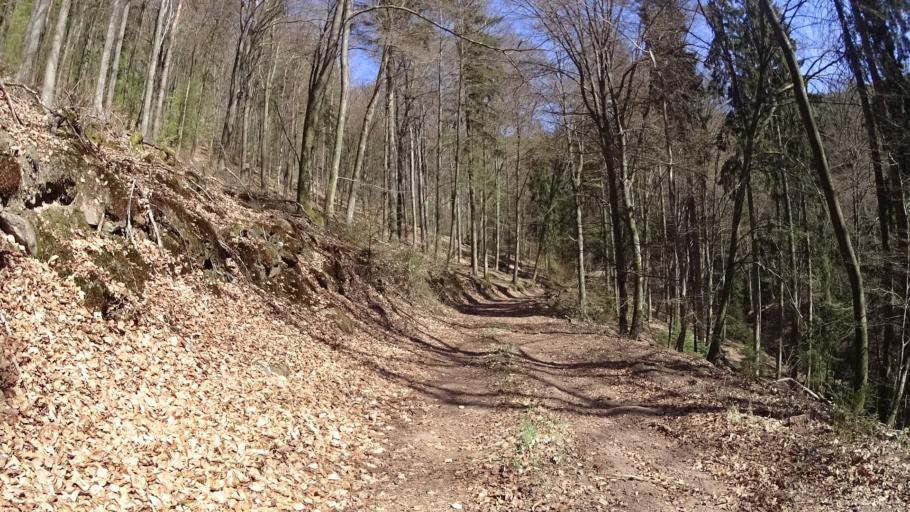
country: DE
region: Rheinland-Pfalz
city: Lambrecht
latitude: 49.3907
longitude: 8.0679
